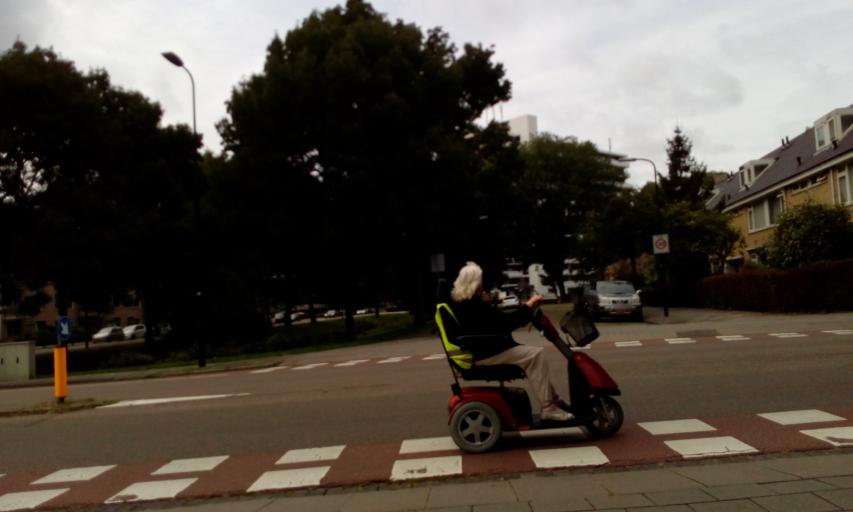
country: NL
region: South Holland
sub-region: Gemeente Rijswijk
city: Rijswijk
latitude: 52.0340
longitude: 4.3203
